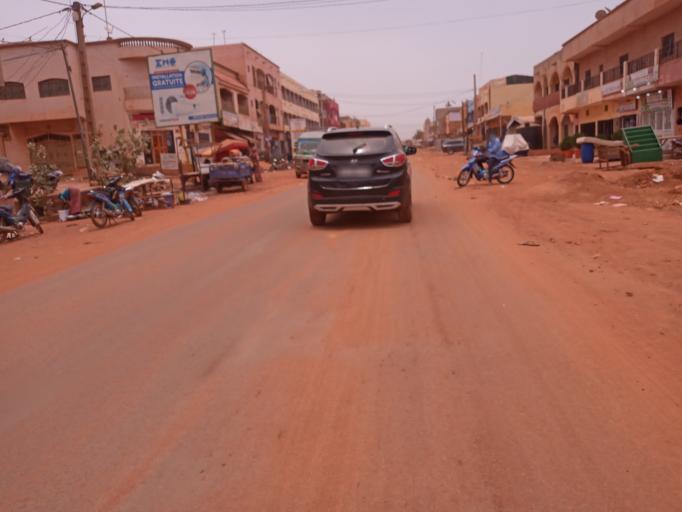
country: ML
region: Bamako
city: Bamako
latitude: 12.5807
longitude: -8.0186
